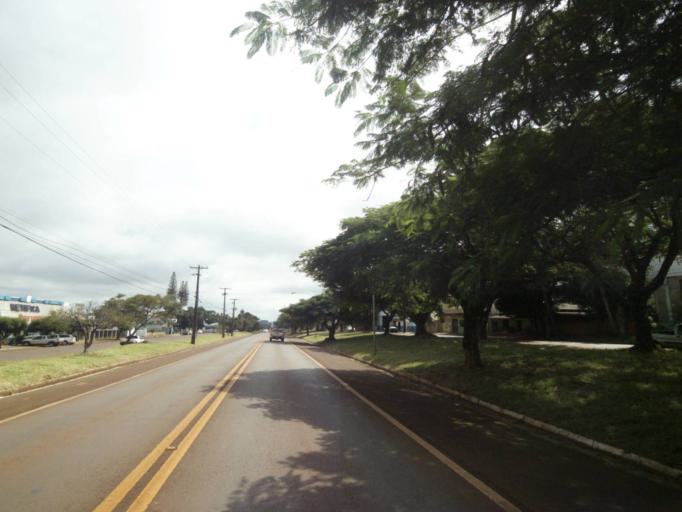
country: BR
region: Parana
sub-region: Campo Mourao
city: Campo Mourao
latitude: -24.0244
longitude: -52.3646
